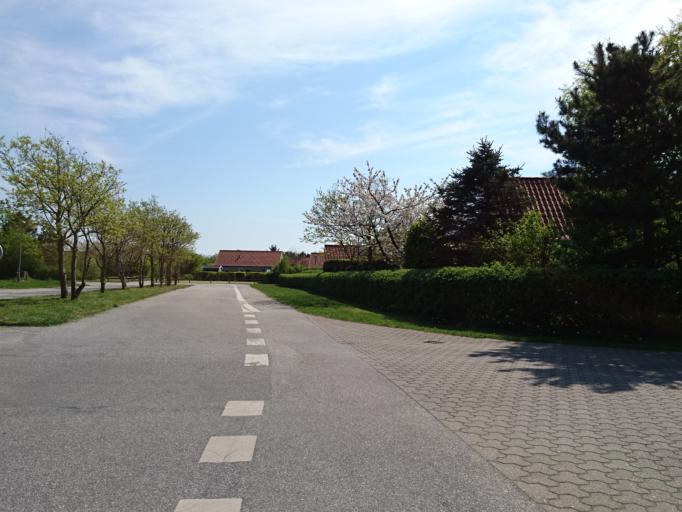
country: DK
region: North Denmark
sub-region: Frederikshavn Kommune
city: Skagen
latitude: 57.7338
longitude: 10.5969
